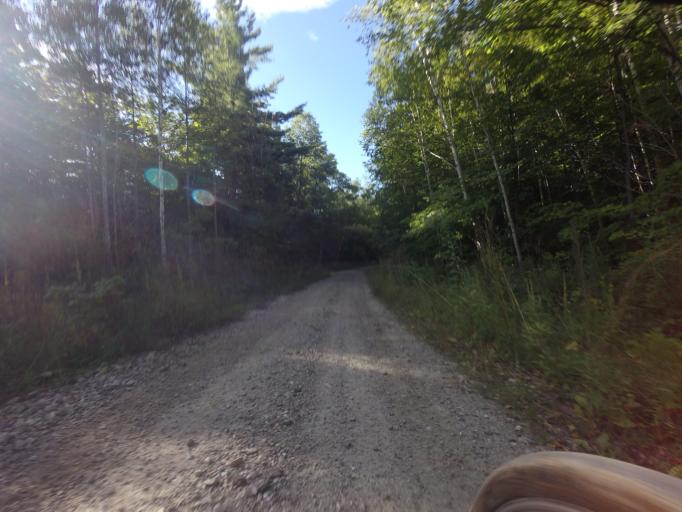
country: CA
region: Ontario
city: Arnprior
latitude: 45.1959
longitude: -76.5219
